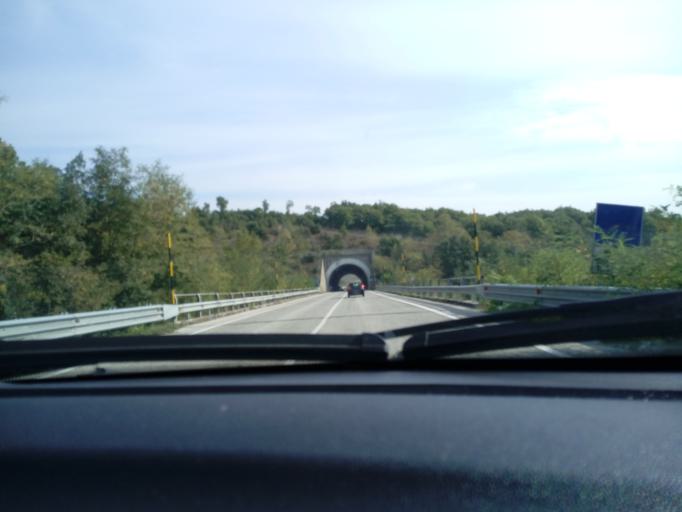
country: IT
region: Molise
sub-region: Provincia di Campobasso
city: Gambatesa
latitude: 41.5273
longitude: 14.8712
